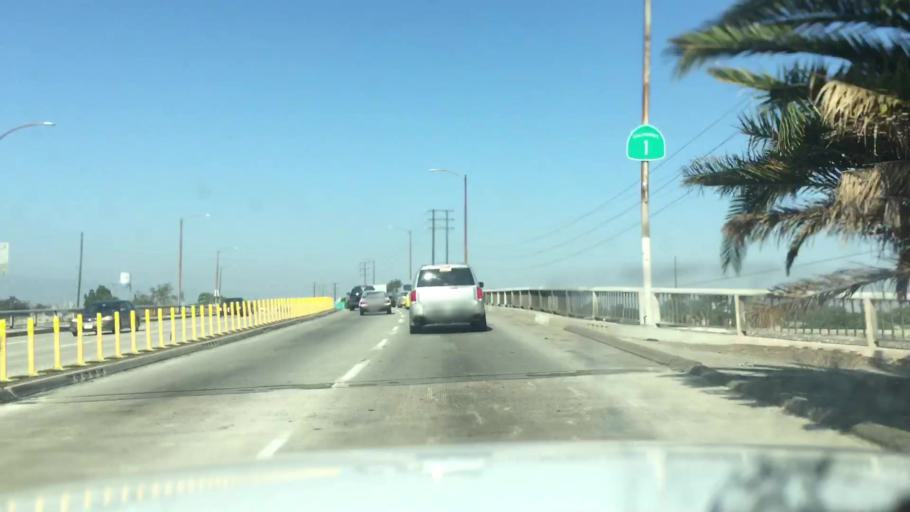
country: US
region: California
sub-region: Los Angeles County
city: Long Beach
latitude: 33.7903
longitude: -118.2044
